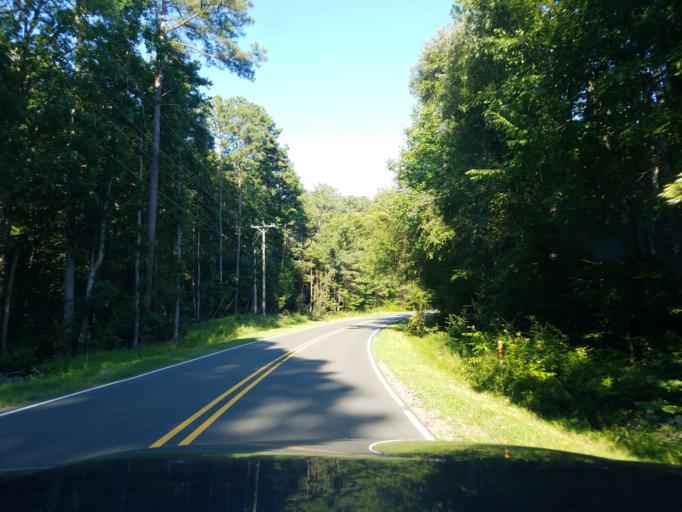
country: US
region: North Carolina
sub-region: Wake County
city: Green Level
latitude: 35.8763
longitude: -78.9406
